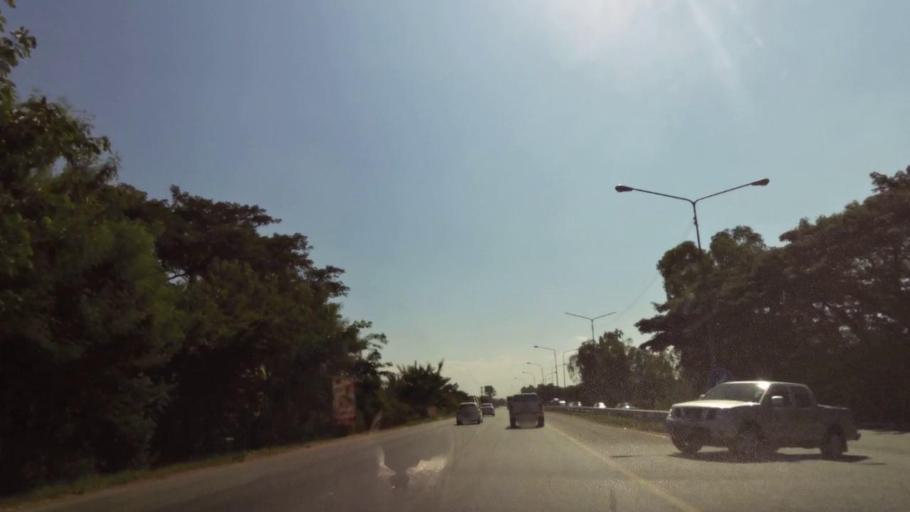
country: TH
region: Nakhon Sawan
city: Nakhon Sawan
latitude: 15.7814
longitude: 100.1211
